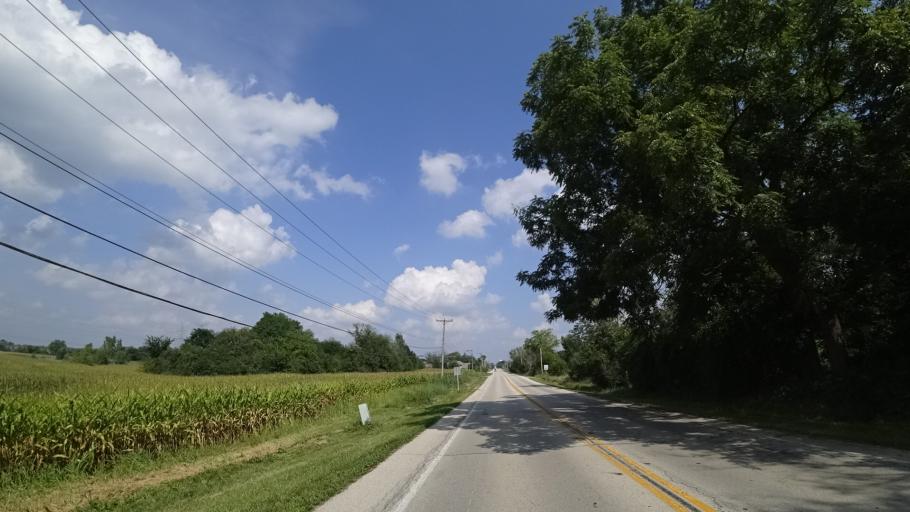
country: US
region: Illinois
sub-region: Cook County
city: Orland Park
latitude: 41.6517
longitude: -87.8877
